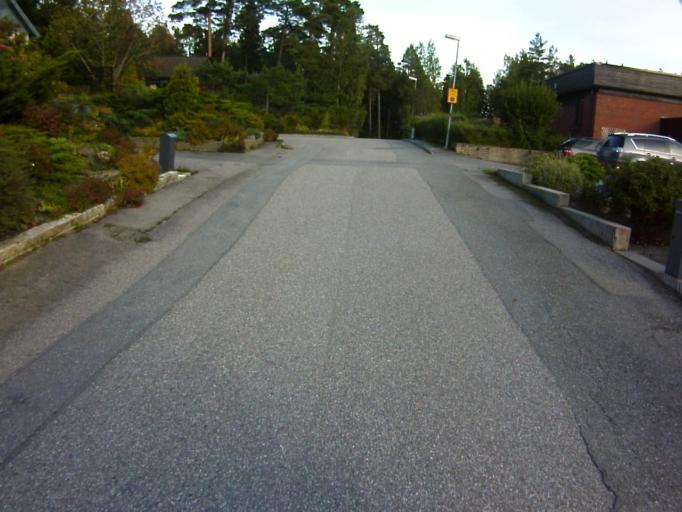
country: SE
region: Soedermanland
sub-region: Eskilstuna Kommun
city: Eskilstuna
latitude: 59.3871
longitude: 16.5472
